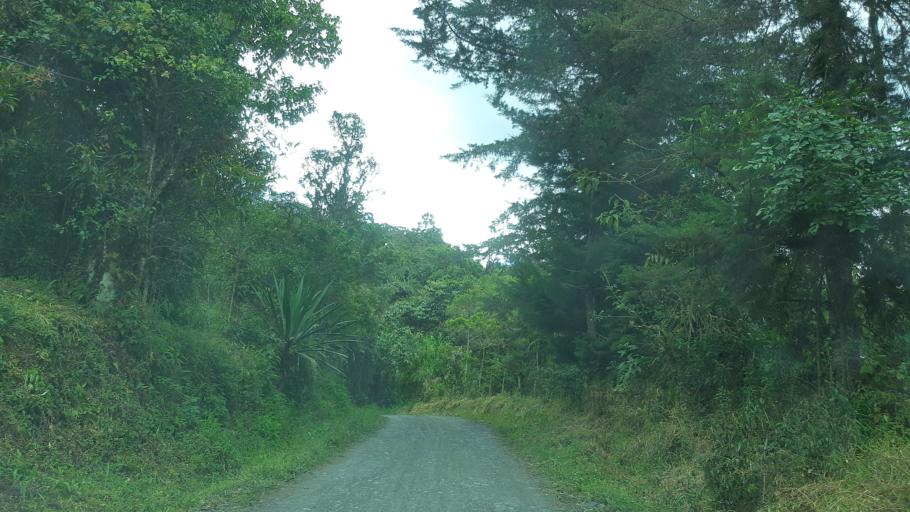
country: CO
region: Boyaca
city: Garagoa
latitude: 5.0160
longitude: -73.3333
